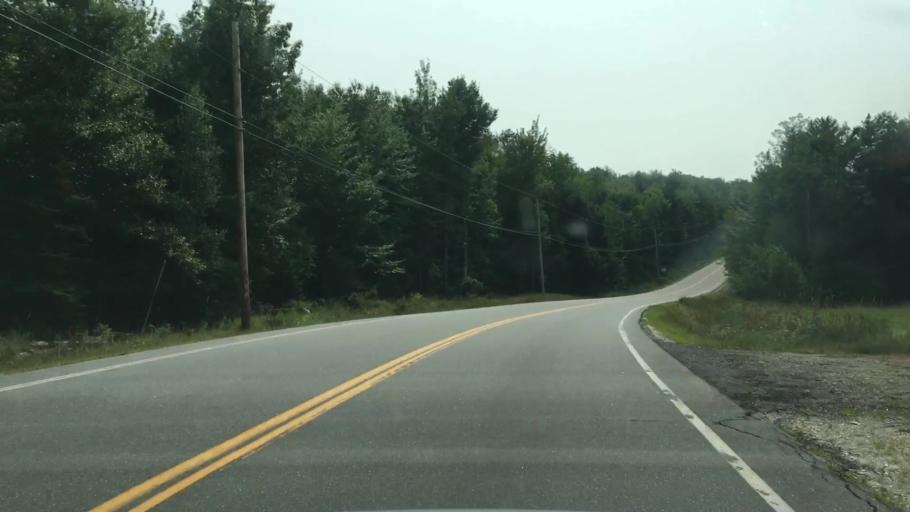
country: US
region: Maine
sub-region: Oxford County
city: Buckfield
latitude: 44.2656
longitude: -70.4245
